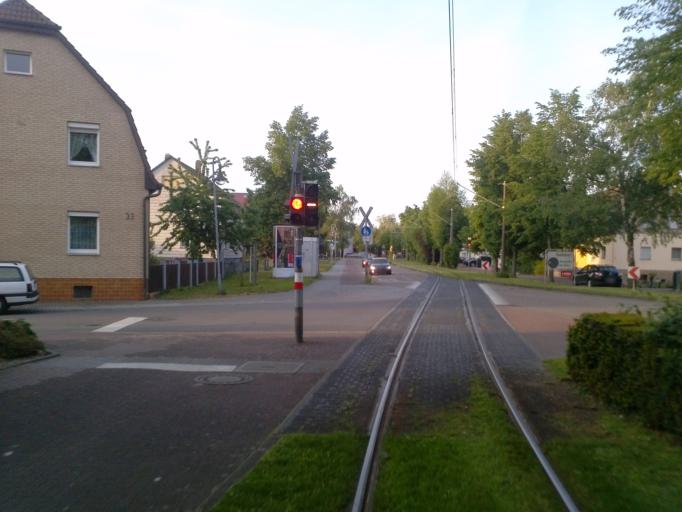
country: DE
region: Baden-Wuerttemberg
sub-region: Karlsruhe Region
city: Rheinstetten
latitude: 48.9764
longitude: 8.3140
